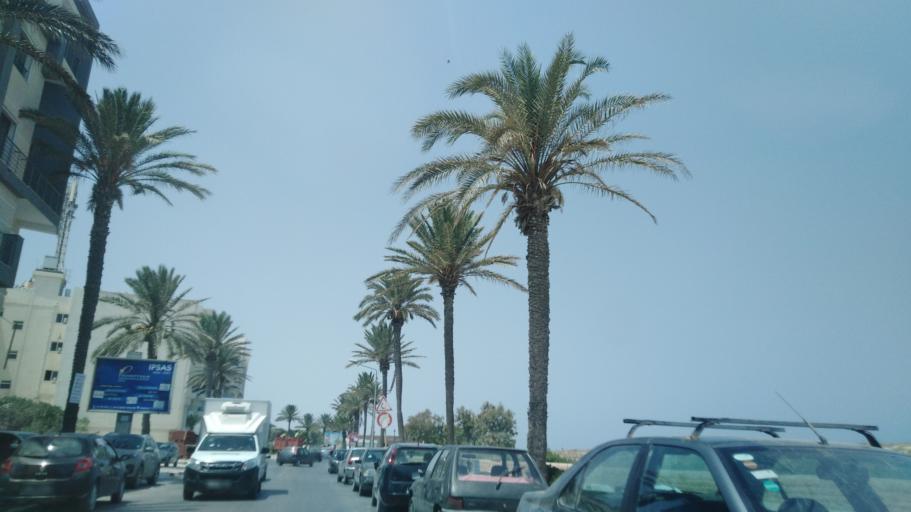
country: TN
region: Al Mahdiyah
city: Mahdia
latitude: 35.5104
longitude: 11.0536
